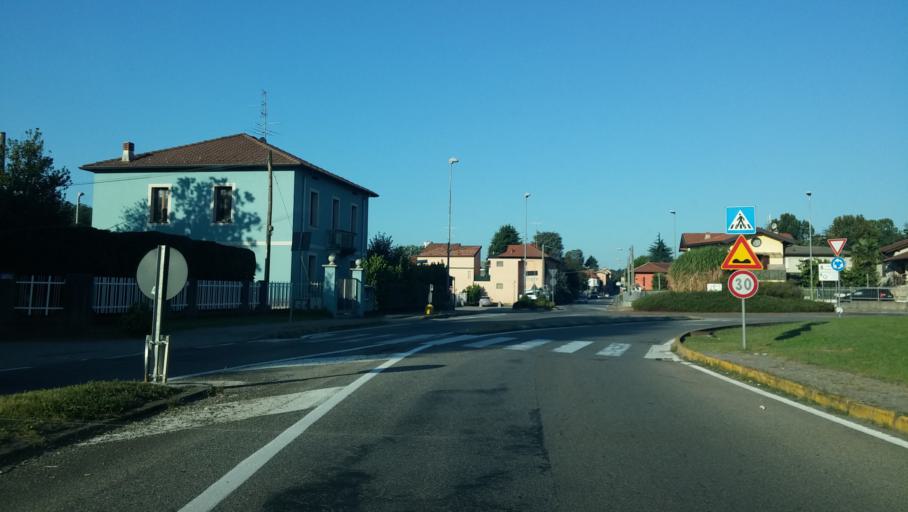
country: IT
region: Lombardy
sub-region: Provincia di Como
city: Bulgarograsso
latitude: 45.7514
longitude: 9.0140
